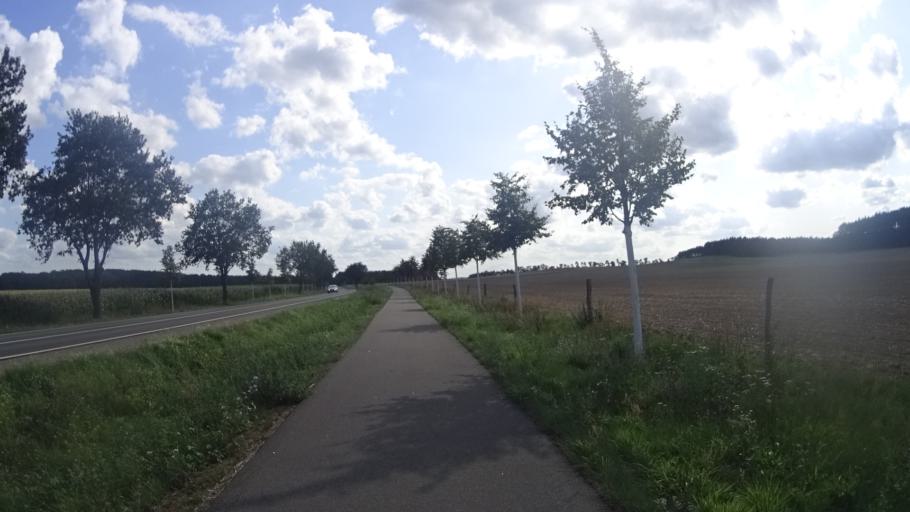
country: DE
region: Brandenburg
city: Rhinow
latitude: 52.6979
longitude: 12.3679
